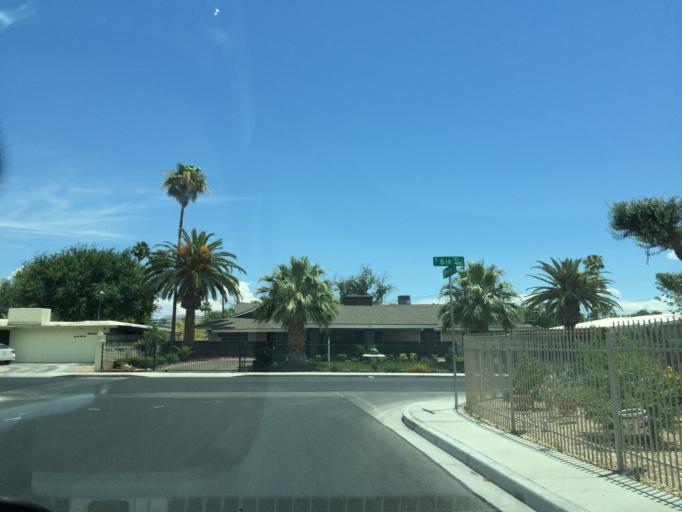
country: US
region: Nevada
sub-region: Clark County
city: Las Vegas
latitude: 36.1539
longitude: -115.1466
